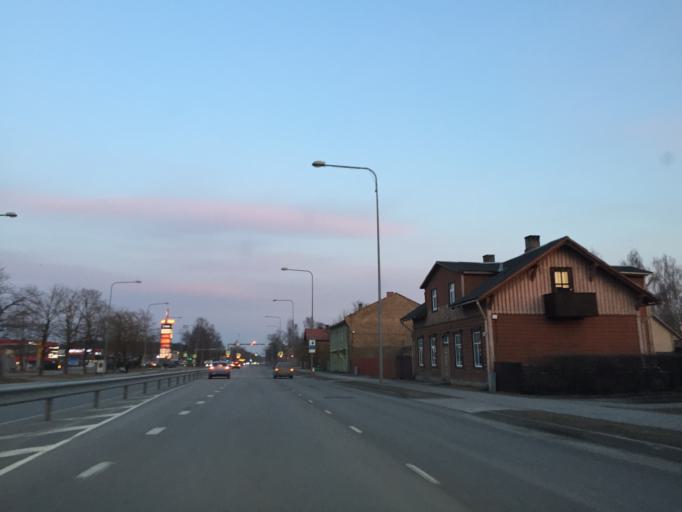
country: EE
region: Paernumaa
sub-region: Paernu linn
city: Parnu
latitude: 58.3713
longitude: 24.5452
